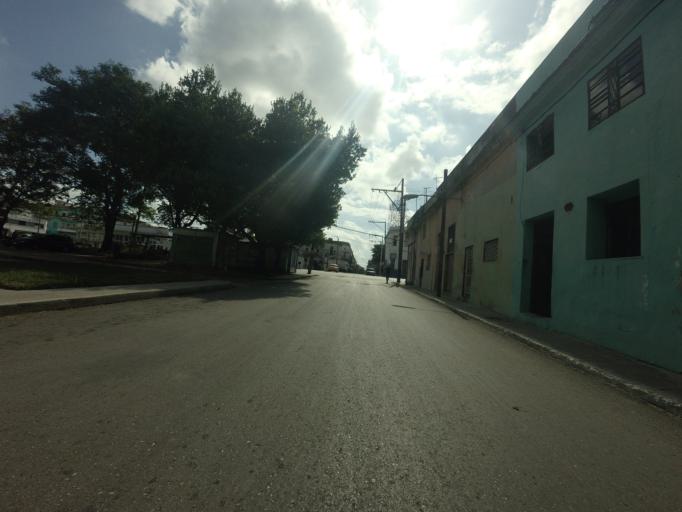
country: CU
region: La Habana
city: Havana
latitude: 23.1340
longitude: -82.3765
